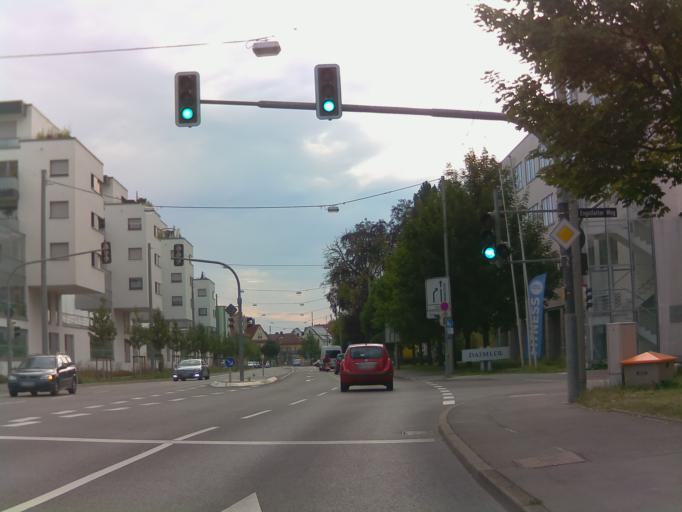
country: DE
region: Baden-Wuerttemberg
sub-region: Regierungsbezirk Stuttgart
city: Leinfelden-Echterdingen
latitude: 48.7282
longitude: 9.1352
